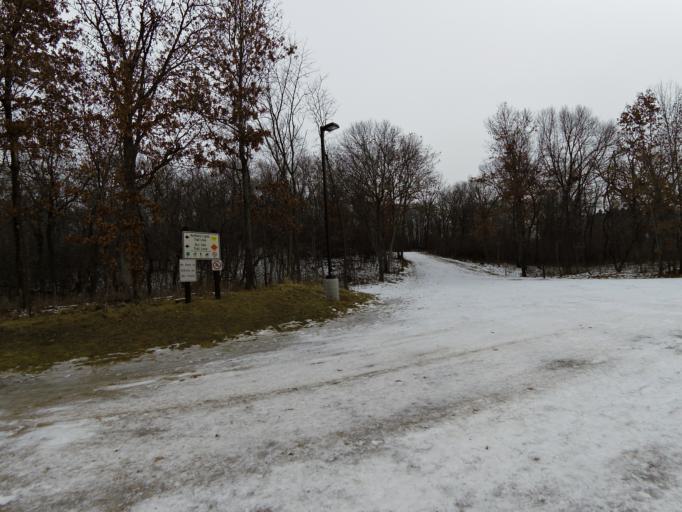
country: US
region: Minnesota
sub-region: Washington County
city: Lake Elmo
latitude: 44.9772
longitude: -92.9019
